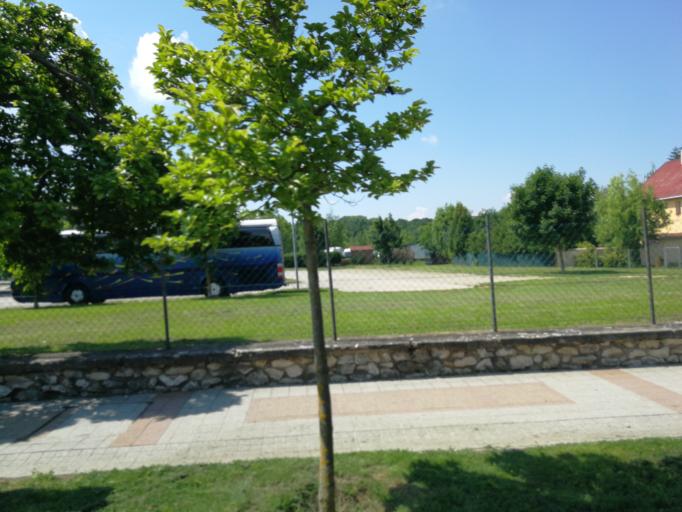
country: HU
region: Vas
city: Sarvar
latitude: 47.2490
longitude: 16.9474
